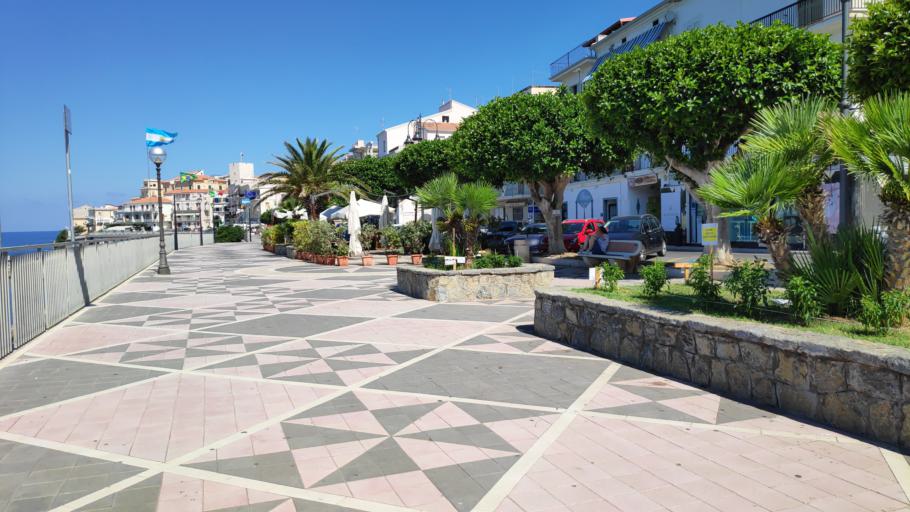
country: IT
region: Calabria
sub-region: Provincia di Cosenza
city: Diamante
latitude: 39.6765
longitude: 15.8193
